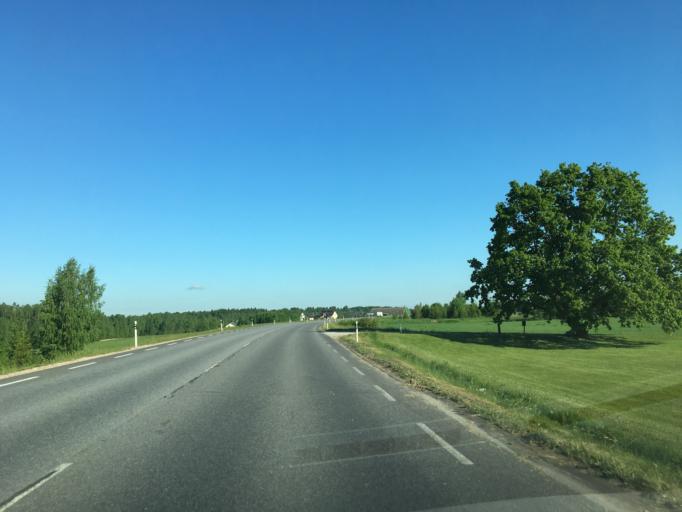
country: EE
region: Tartu
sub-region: Tartu linn
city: Tartu
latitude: 58.4295
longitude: 26.6846
